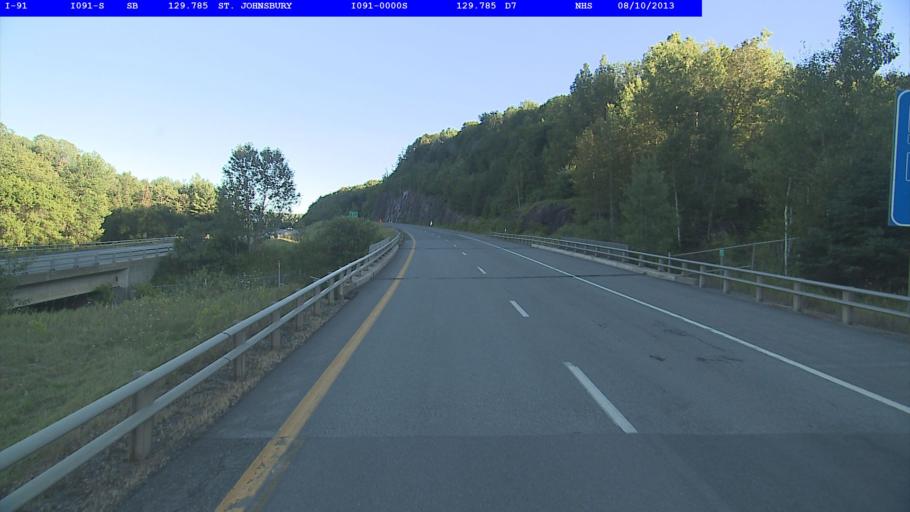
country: US
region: Vermont
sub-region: Caledonia County
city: Saint Johnsbury
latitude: 44.4160
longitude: -72.0315
